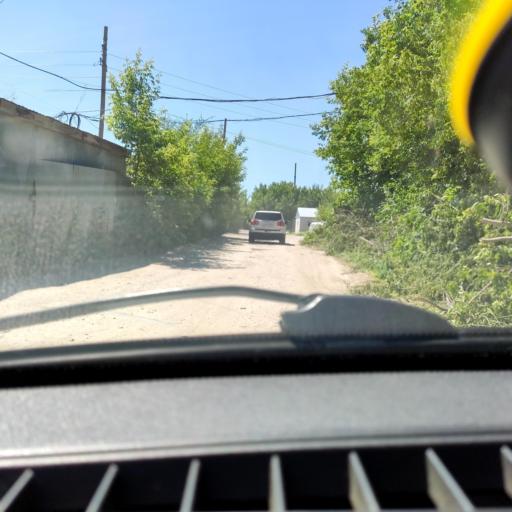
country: RU
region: Samara
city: Tol'yatti
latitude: 53.5690
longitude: 49.2985
